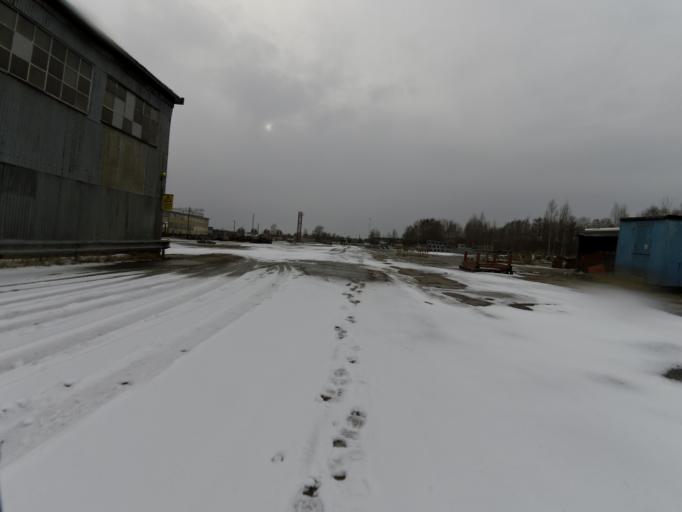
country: SE
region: Gaevleborg
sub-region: Gavle Kommun
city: Gavle
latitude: 60.6849
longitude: 17.1702
